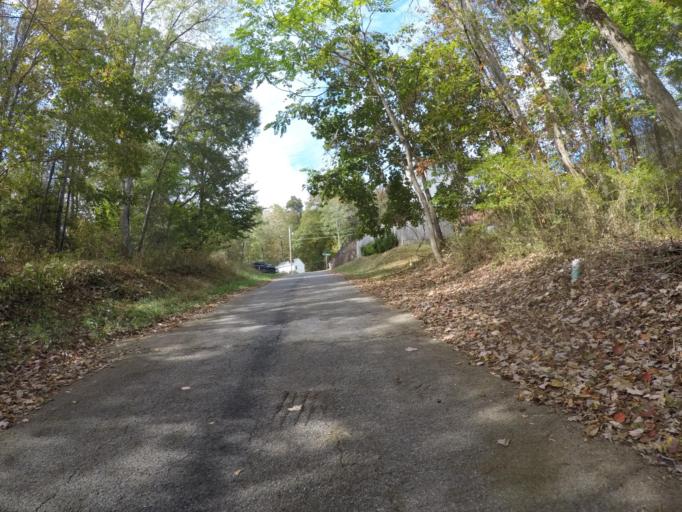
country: US
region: West Virginia
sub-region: Cabell County
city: Huntington
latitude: 38.3959
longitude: -82.3904
